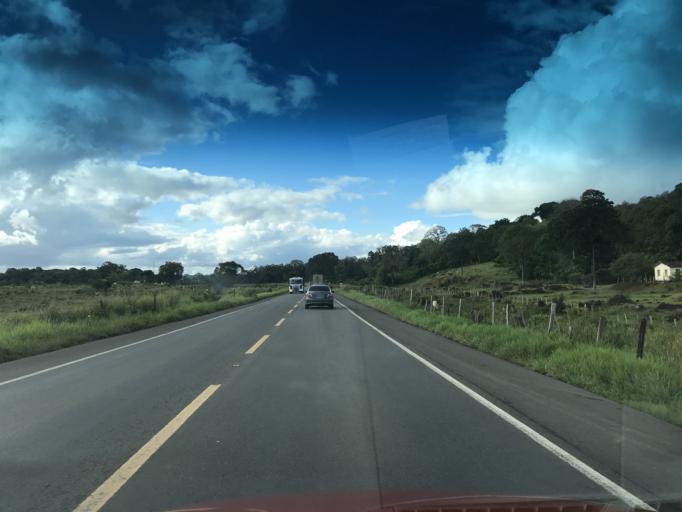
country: BR
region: Bahia
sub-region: Ibirapitanga
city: Ibirapitanga
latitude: -14.1595
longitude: -39.3278
